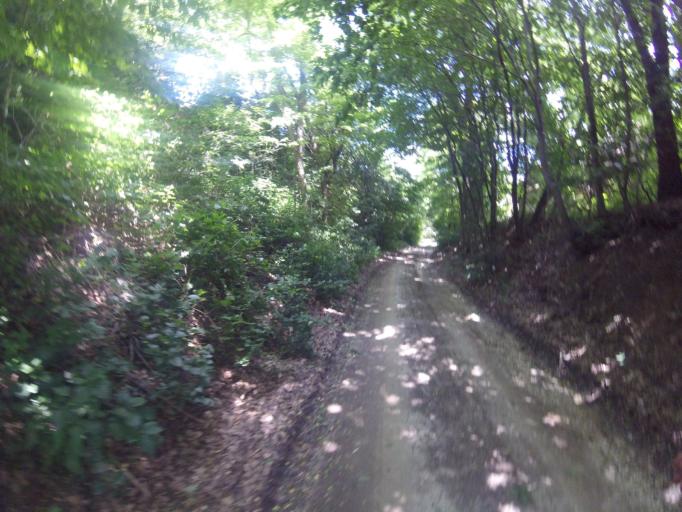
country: HU
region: Zala
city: Zalalovo
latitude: 46.8328
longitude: 16.5601
